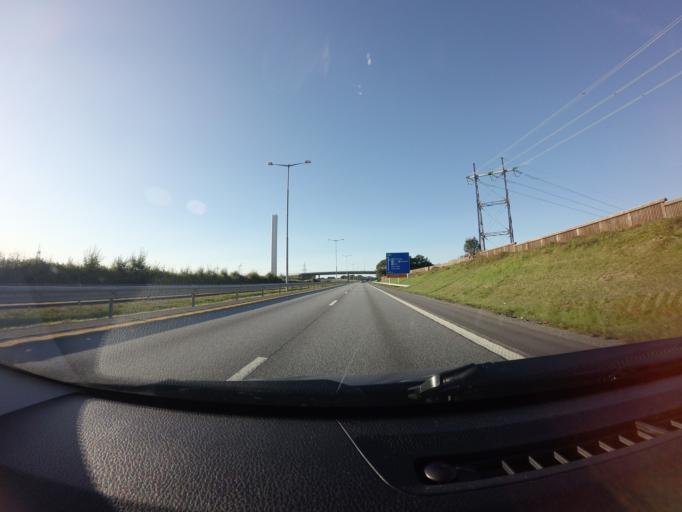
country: NO
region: Rogaland
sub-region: Sola
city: Sola
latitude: 58.9050
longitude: 5.7022
